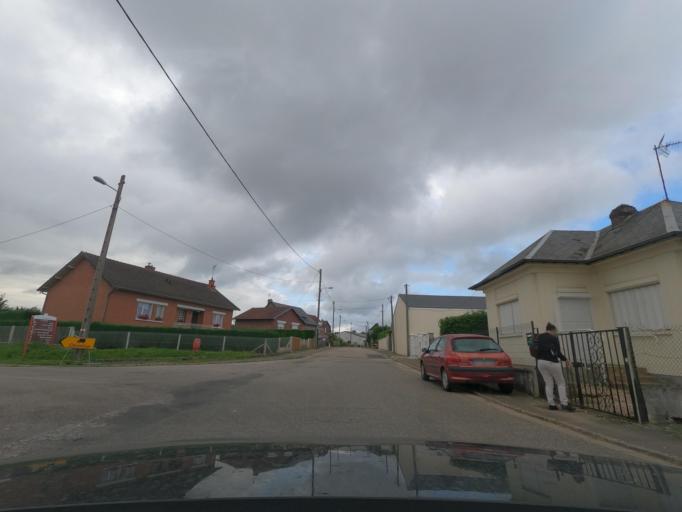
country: FR
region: Haute-Normandie
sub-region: Departement de la Seine-Maritime
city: Forges-les-Eaux
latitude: 49.6125
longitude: 1.5526
